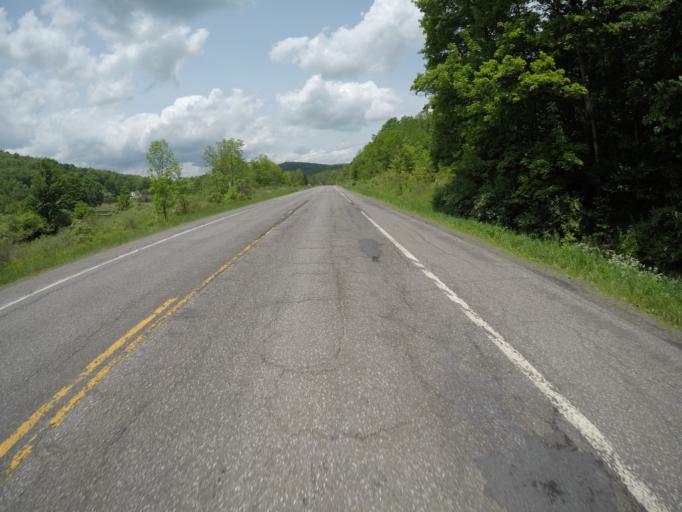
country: US
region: New York
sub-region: Delaware County
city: Stamford
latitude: 42.2204
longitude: -74.5923
